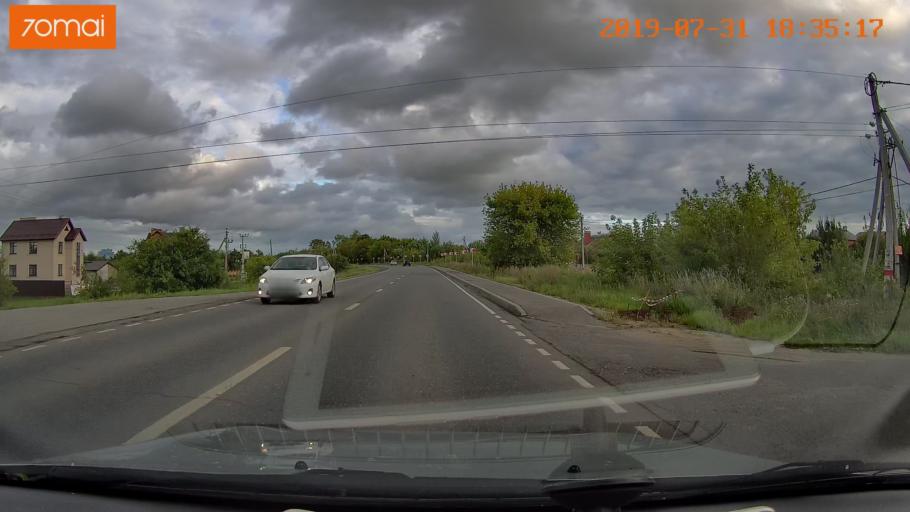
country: RU
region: Moskovskaya
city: Voskresensk
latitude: 55.2962
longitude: 38.6674
